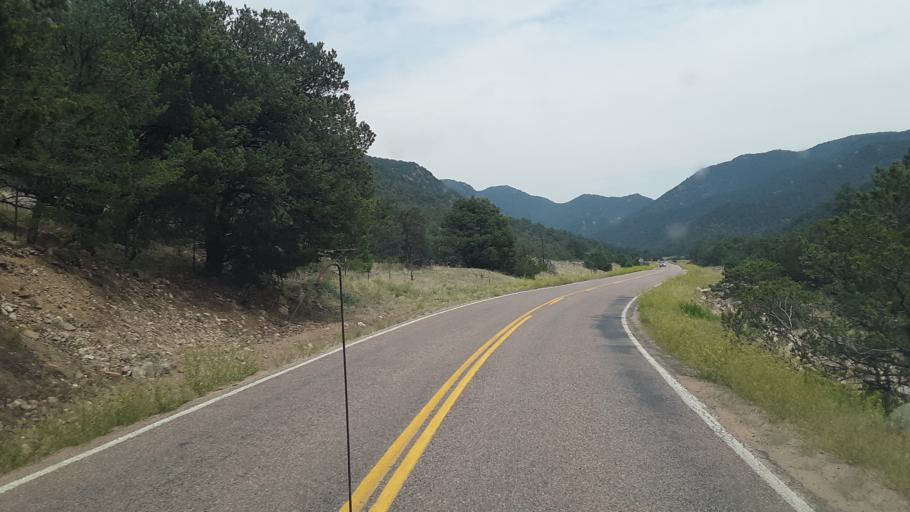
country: US
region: Colorado
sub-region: Fremont County
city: Canon City
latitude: 38.4128
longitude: -105.4349
